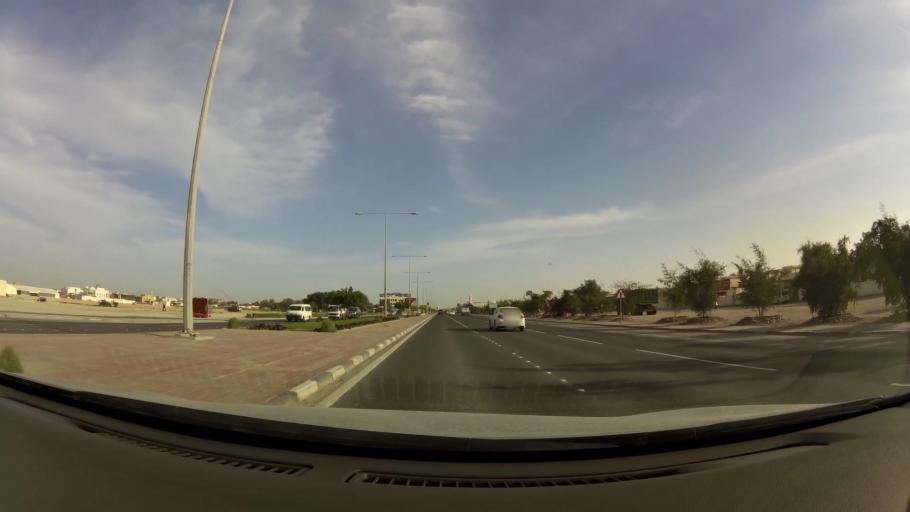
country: QA
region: Al Wakrah
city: Al Wakrah
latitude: 25.1856
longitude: 51.6002
